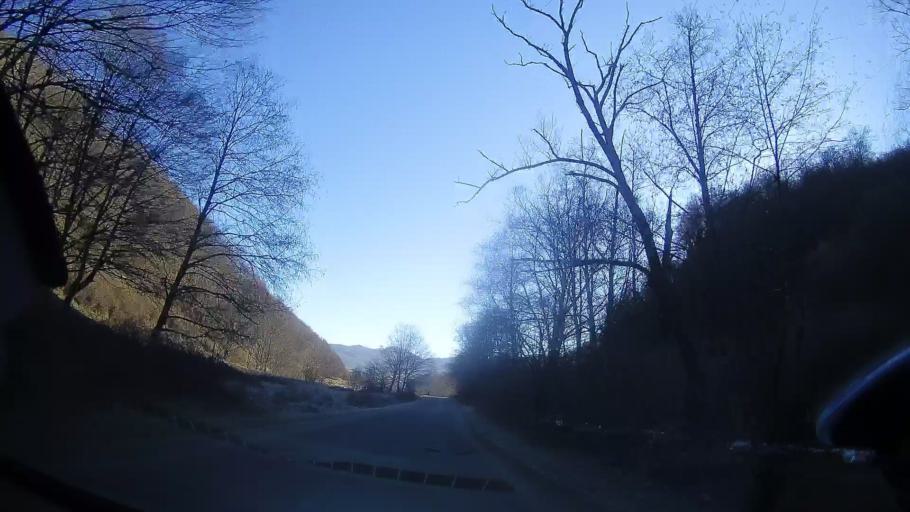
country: RO
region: Cluj
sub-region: Comuna Sacueu
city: Sacuieu
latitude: 46.8328
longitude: 22.8650
